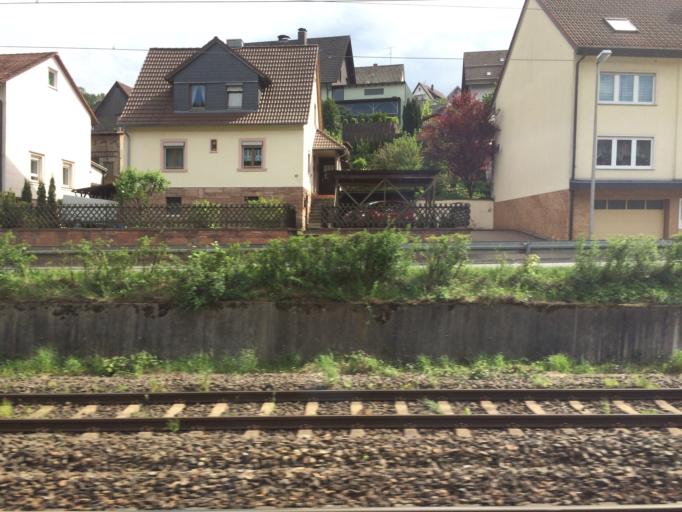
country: DE
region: Bavaria
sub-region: Regierungsbezirk Unterfranken
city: Heigenbrucken
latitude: 50.0273
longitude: 9.3716
